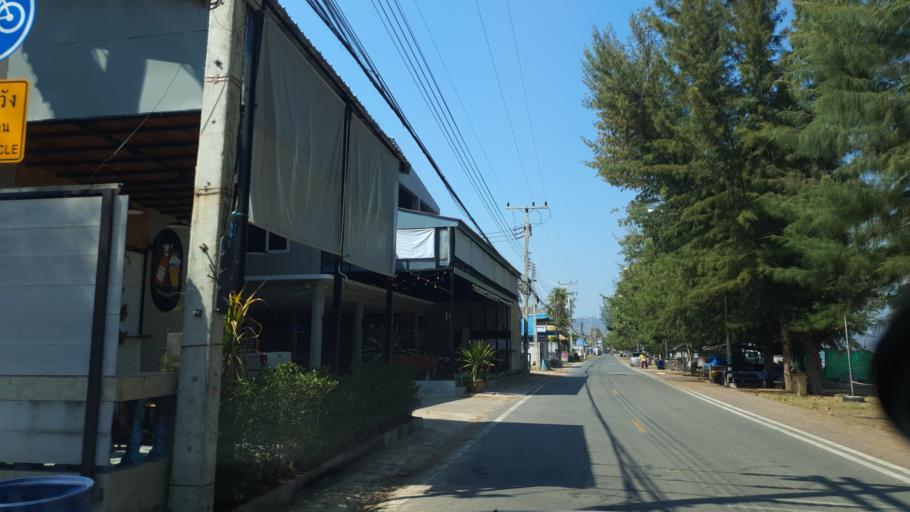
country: TH
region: Prachuap Khiri Khan
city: Sam Roi Yot
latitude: 12.2344
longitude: 99.9921
